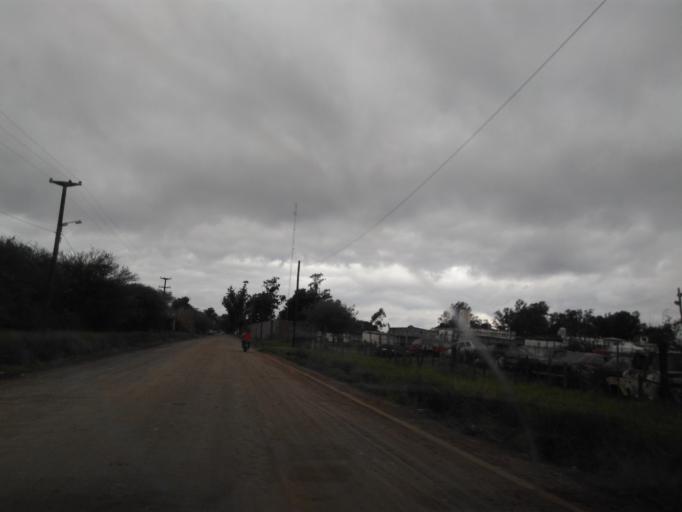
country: AR
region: Chaco
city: Fontana
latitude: -27.4538
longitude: -59.0409
